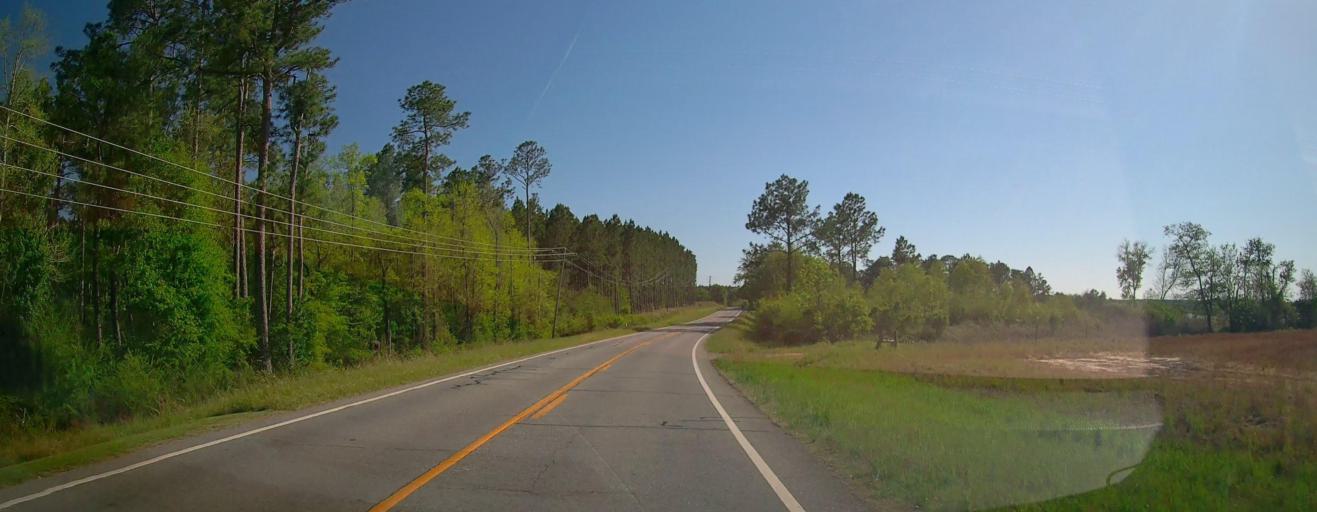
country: US
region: Georgia
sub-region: Wilcox County
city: Rochelle
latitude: 31.9205
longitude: -83.4665
